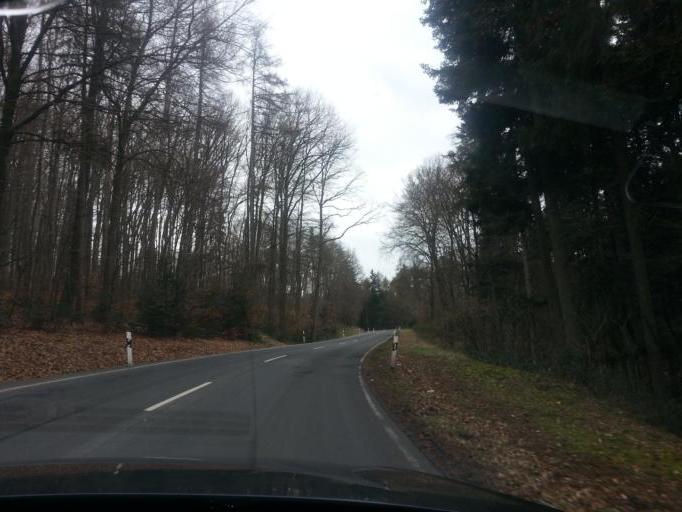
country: DE
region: Rheinland-Pfalz
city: Breitenbach
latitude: 49.3938
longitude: 7.2533
